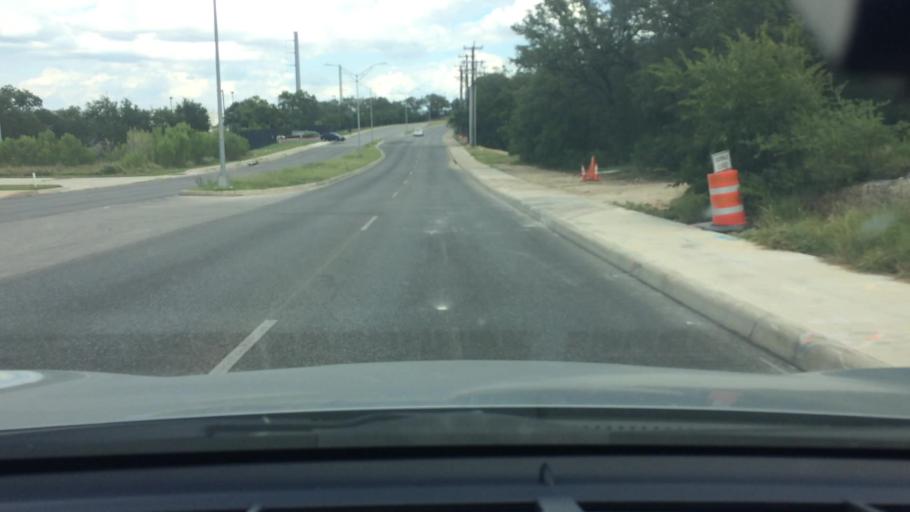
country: US
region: Texas
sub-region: Bexar County
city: Leon Valley
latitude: 29.4796
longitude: -98.6967
